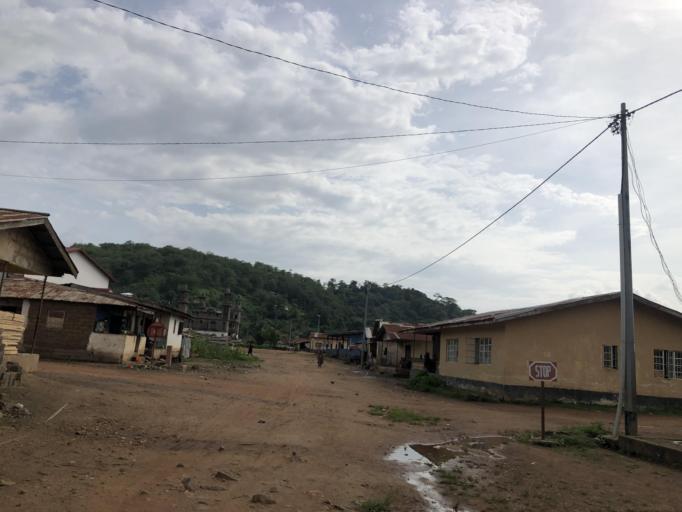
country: SL
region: Northern Province
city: Bumbuna
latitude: 9.0438
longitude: -11.7442
